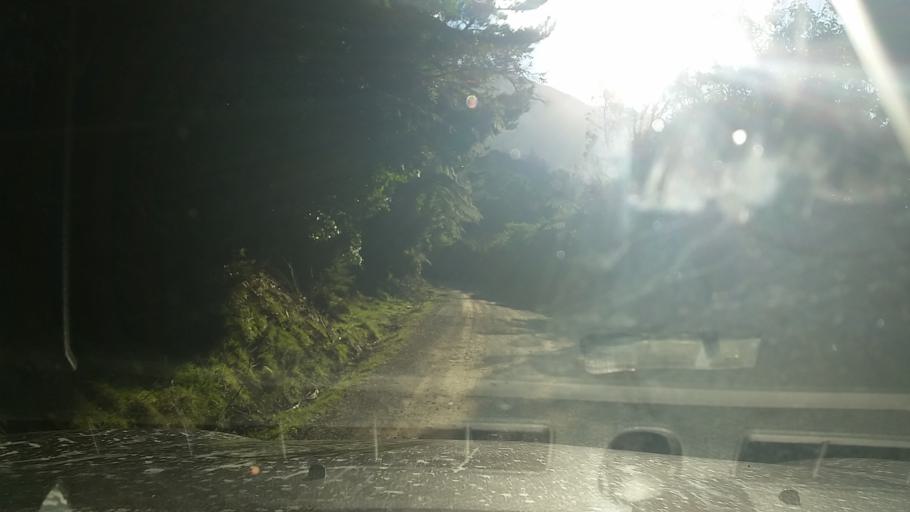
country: NZ
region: Marlborough
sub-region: Marlborough District
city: Picton
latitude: -41.0635
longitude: 174.1170
